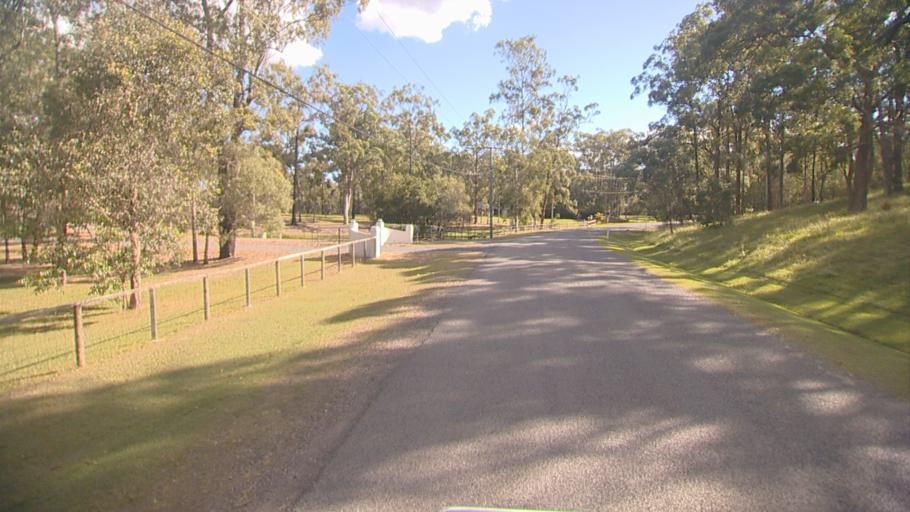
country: AU
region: Queensland
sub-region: Redland
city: Redland Bay
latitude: -27.6497
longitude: 153.2416
